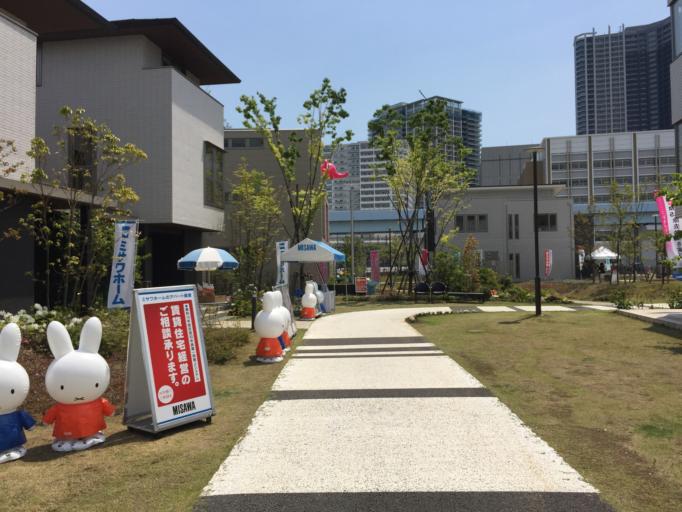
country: JP
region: Tokyo
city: Urayasu
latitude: 35.6508
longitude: 139.7910
